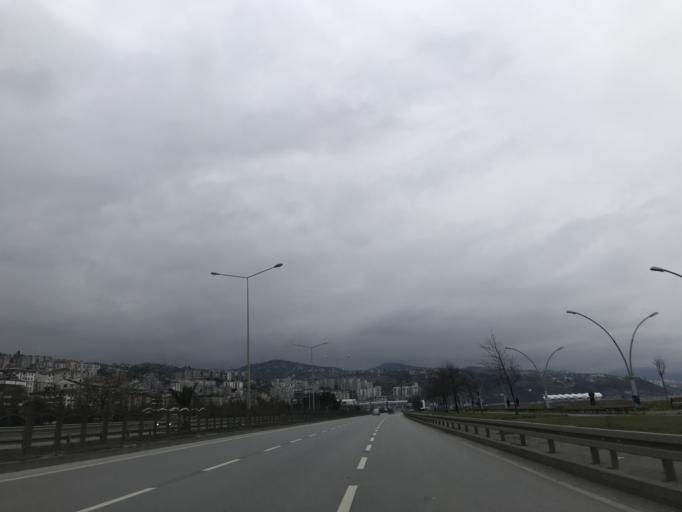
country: TR
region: Trabzon
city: Trabzon
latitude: 41.0000
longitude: 39.6814
